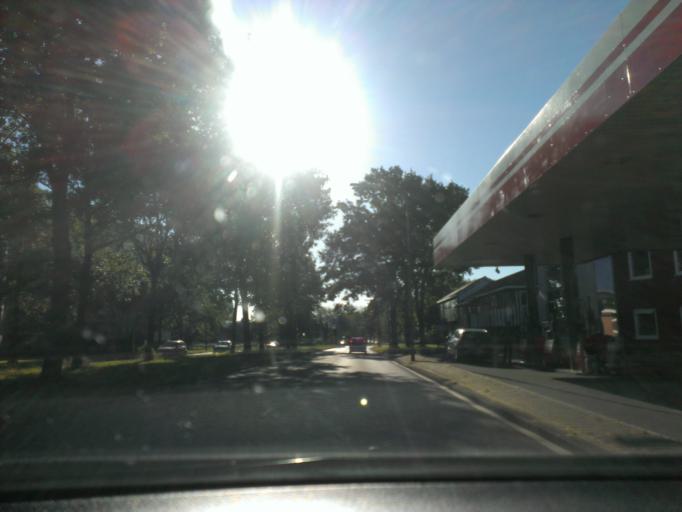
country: NL
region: Drenthe
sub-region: Gemeente Emmen
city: Emmen
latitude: 52.7772
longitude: 6.8945
